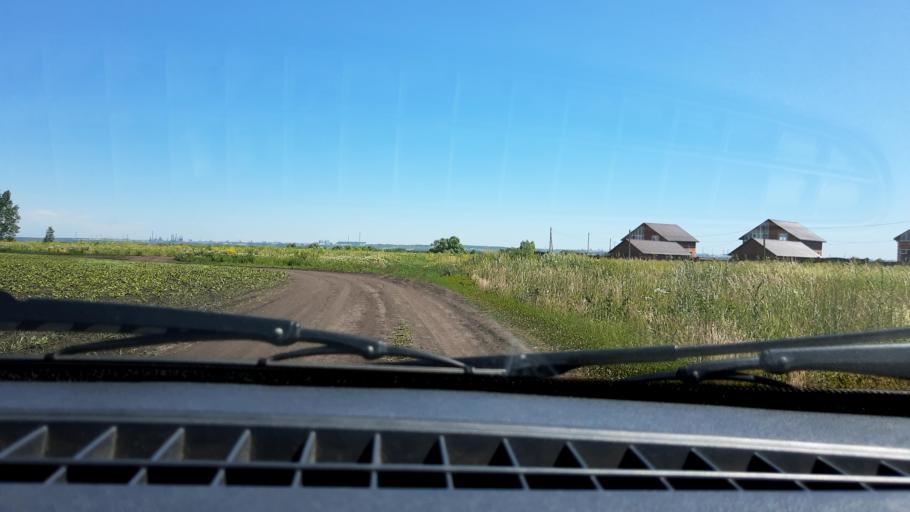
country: RU
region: Bashkortostan
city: Mikhaylovka
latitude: 54.8747
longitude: 55.9315
